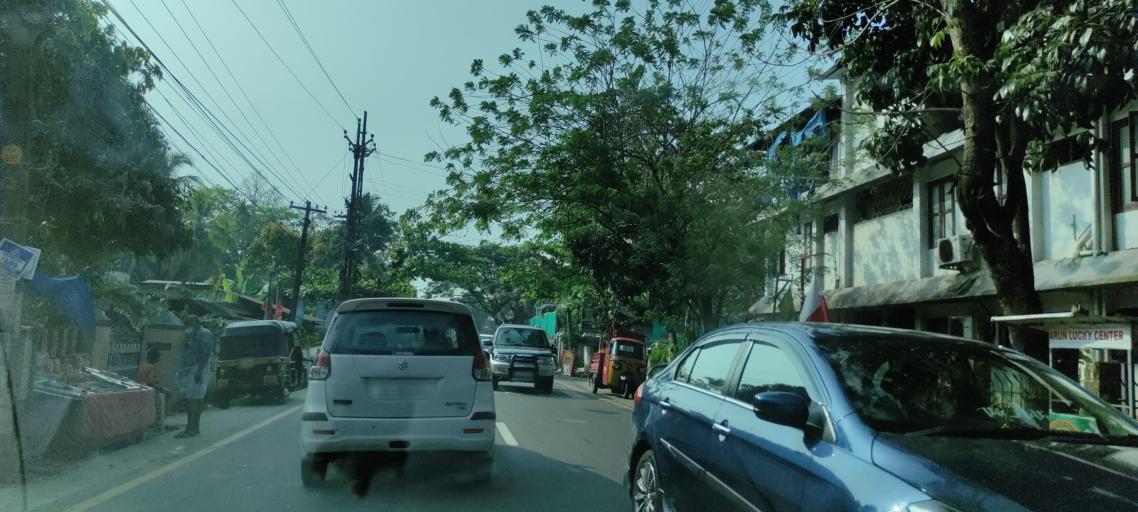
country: IN
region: Kerala
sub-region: Pattanamtitta
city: Tiruvalla
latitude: 9.3712
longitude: 76.5206
